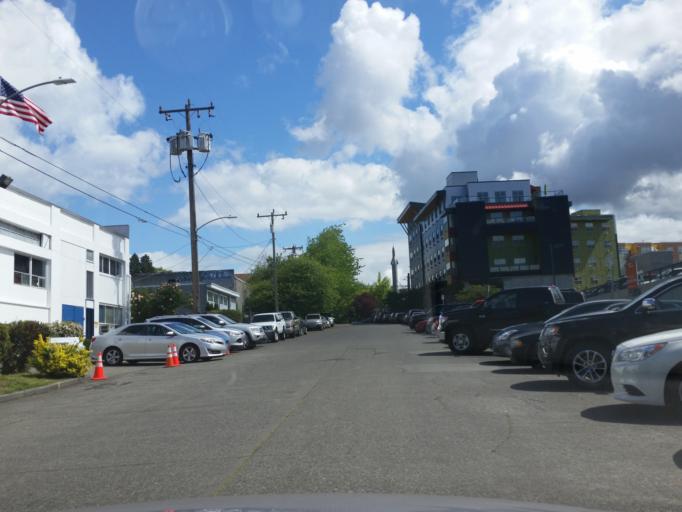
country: US
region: Washington
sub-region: King County
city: Seattle
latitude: 47.6511
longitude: -122.3532
